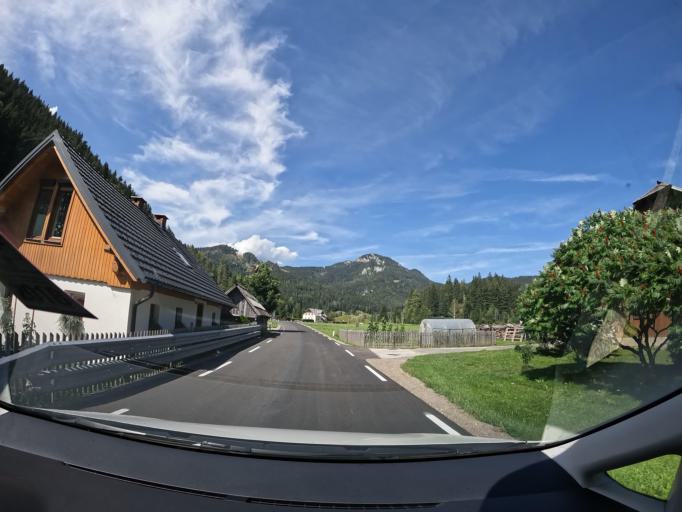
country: AT
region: Carinthia
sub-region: Politischer Bezirk Feldkirchen
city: Feldkirchen in Karnten
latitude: 46.6977
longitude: 14.1183
